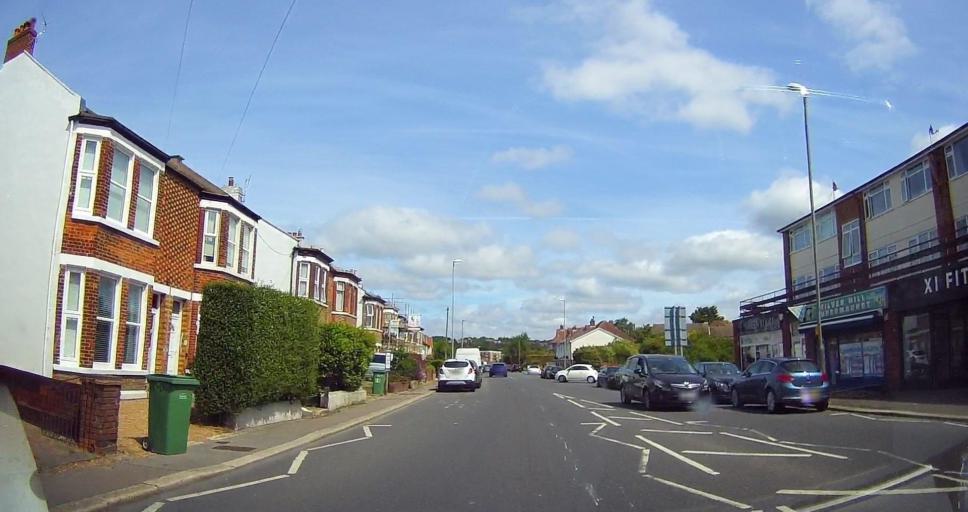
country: GB
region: England
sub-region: East Sussex
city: Saint Leonards-on-Sea
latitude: 50.8713
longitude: 0.5583
